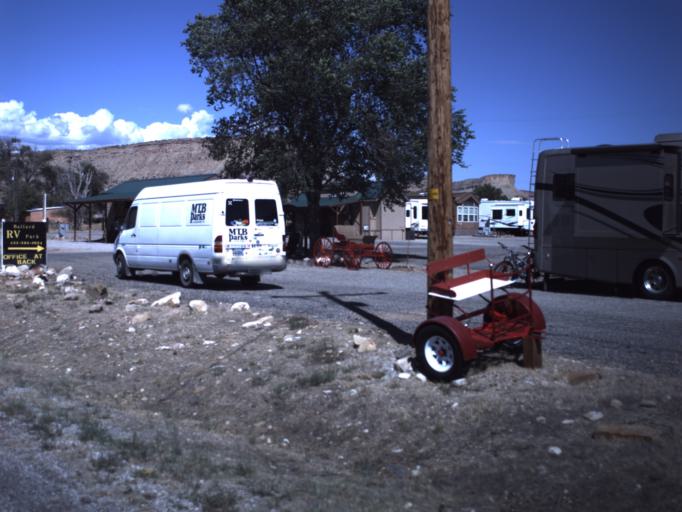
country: US
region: Utah
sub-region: Grand County
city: Moab
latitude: 38.9693
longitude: -109.7151
